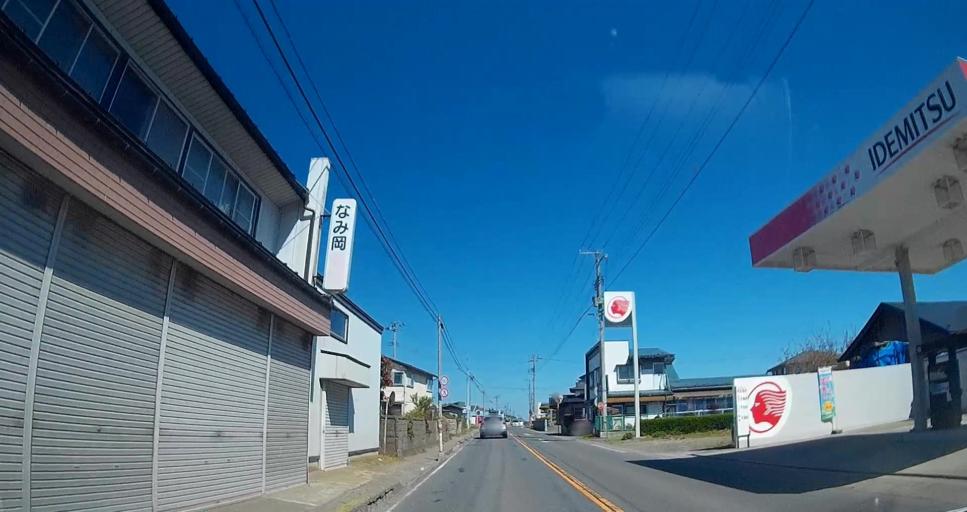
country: JP
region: Aomori
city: Misawa
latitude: 40.6593
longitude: 141.4348
